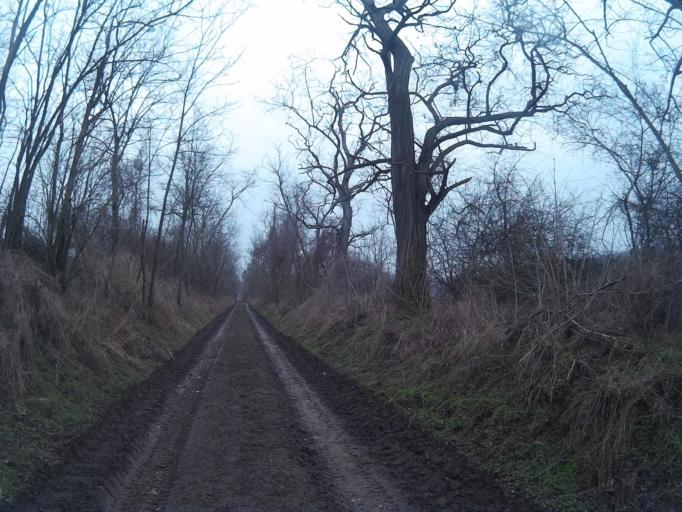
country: HU
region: Fejer
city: Szarliget
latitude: 47.5534
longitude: 18.5602
